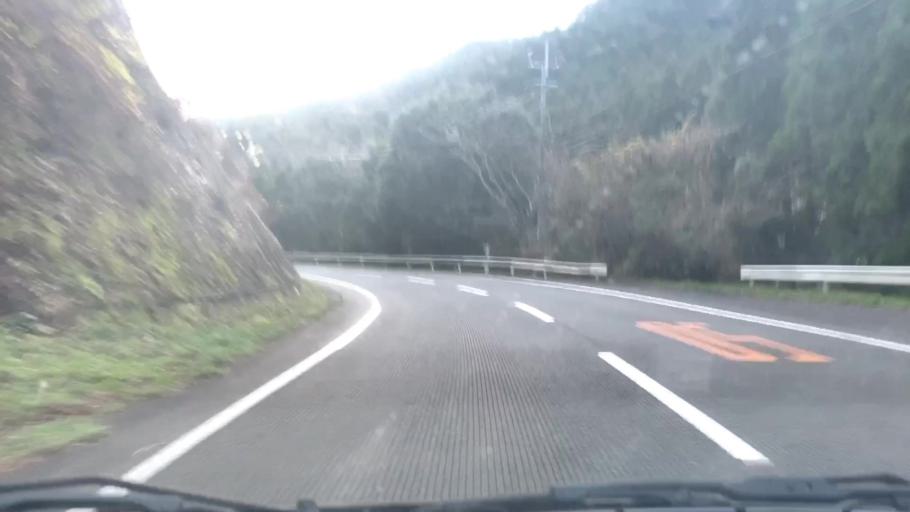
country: JP
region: Saga Prefecture
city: Kashima
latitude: 33.0107
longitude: 130.0629
